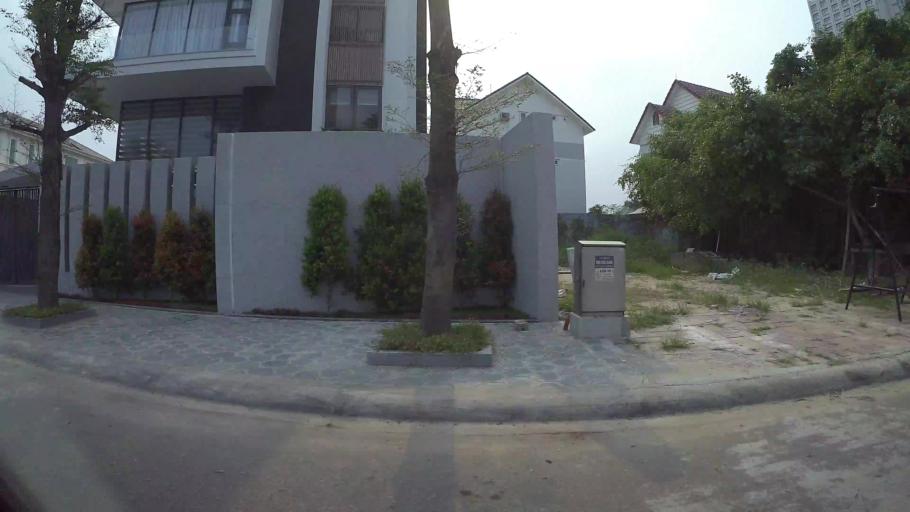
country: VN
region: Da Nang
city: Son Tra
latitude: 16.0472
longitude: 108.2278
